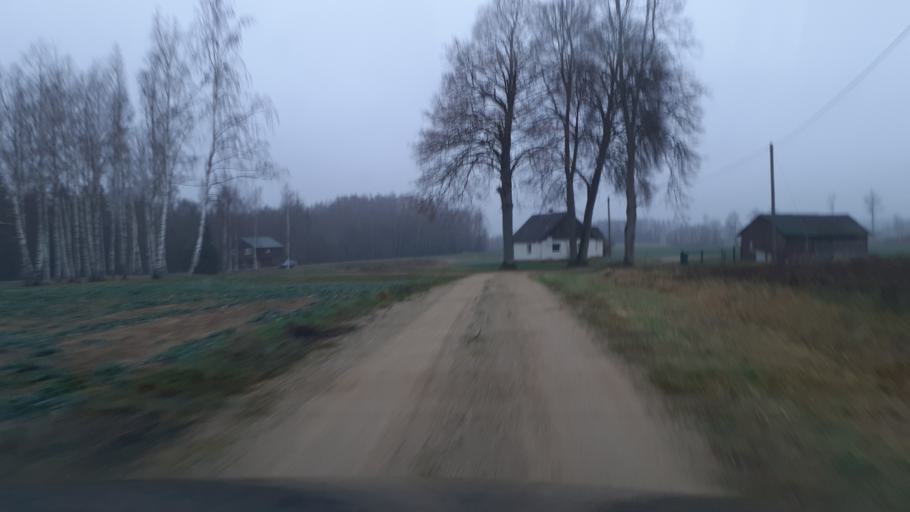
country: LV
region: Alsunga
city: Alsunga
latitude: 56.8928
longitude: 21.6700
